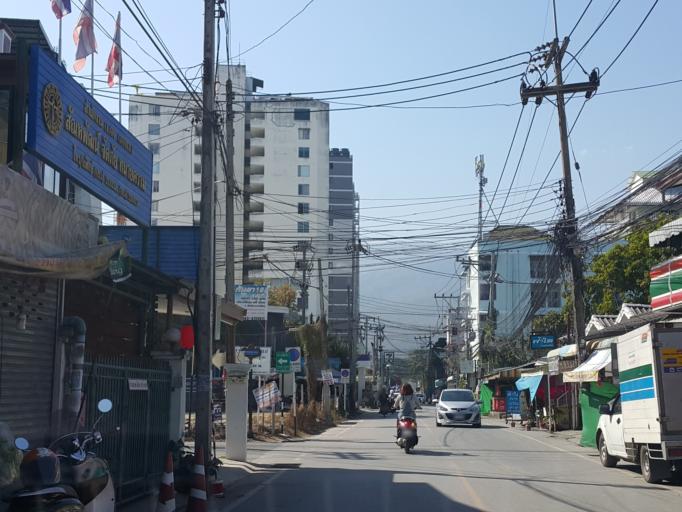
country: TH
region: Chiang Mai
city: Chiang Mai
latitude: 18.8081
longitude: 98.9651
